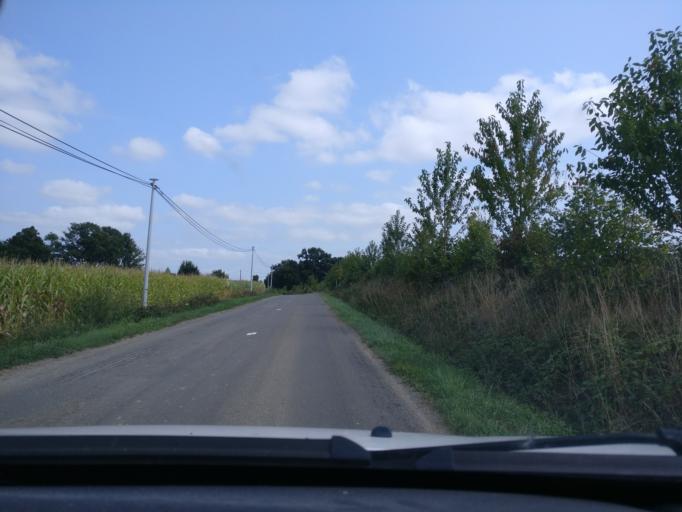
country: FR
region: Brittany
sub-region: Departement d'Ille-et-Vilaine
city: Saint-Sulpice-la-Foret
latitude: 48.2309
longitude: -1.6003
